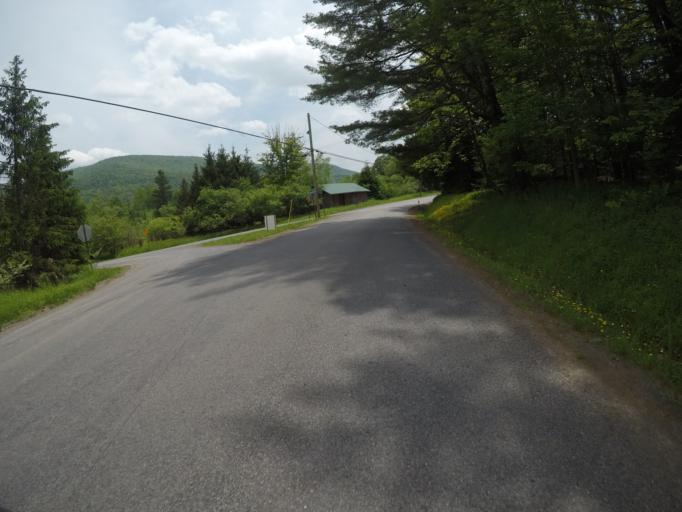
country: US
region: New York
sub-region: Delaware County
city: Stamford
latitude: 42.2148
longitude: -74.6821
